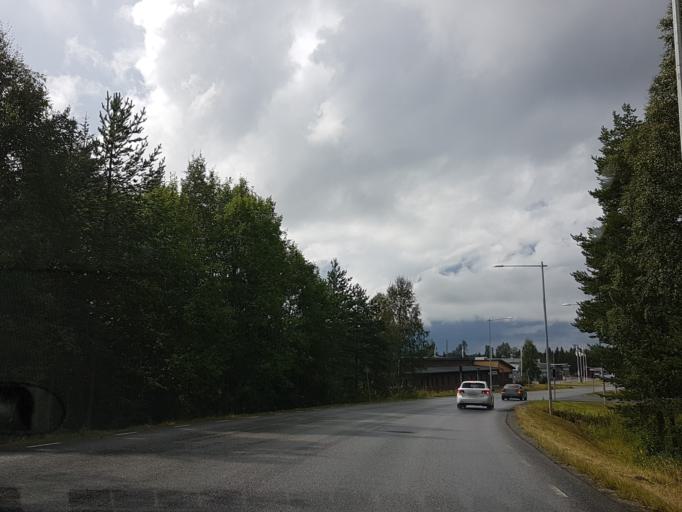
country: SE
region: Vaesterbotten
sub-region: Umea Kommun
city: Ersmark
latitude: 63.8517
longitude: 20.3299
